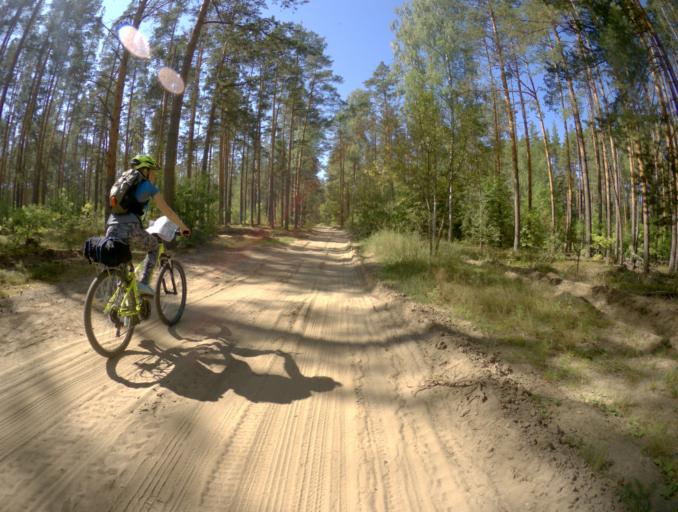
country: RU
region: Vladimir
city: Petushki
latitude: 55.8680
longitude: 39.3874
